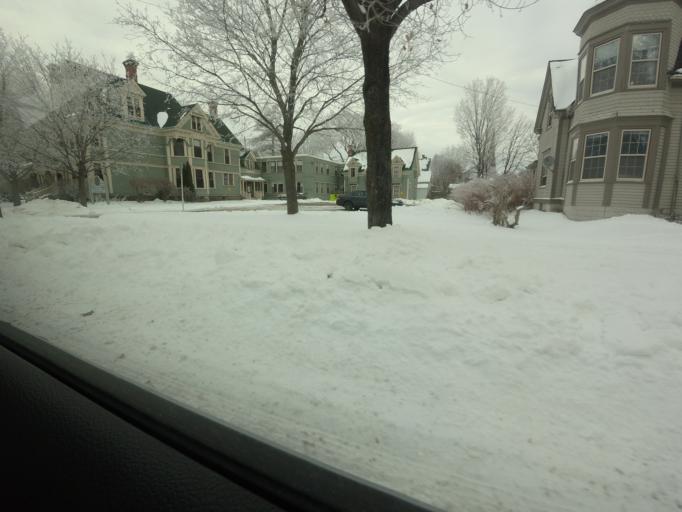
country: CA
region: New Brunswick
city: Fredericton
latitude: 45.9553
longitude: -66.6369
